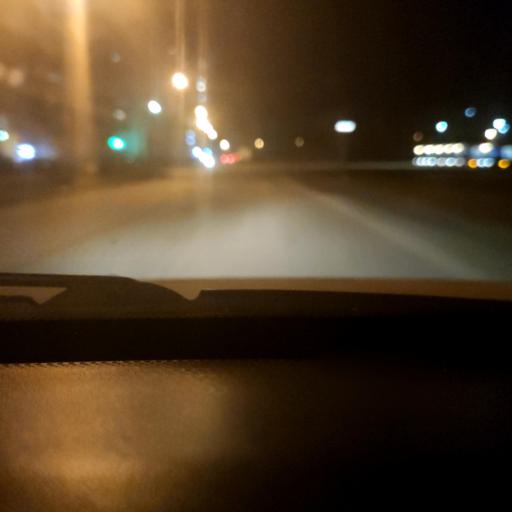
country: RU
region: Perm
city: Polazna
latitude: 58.1328
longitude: 56.3923
